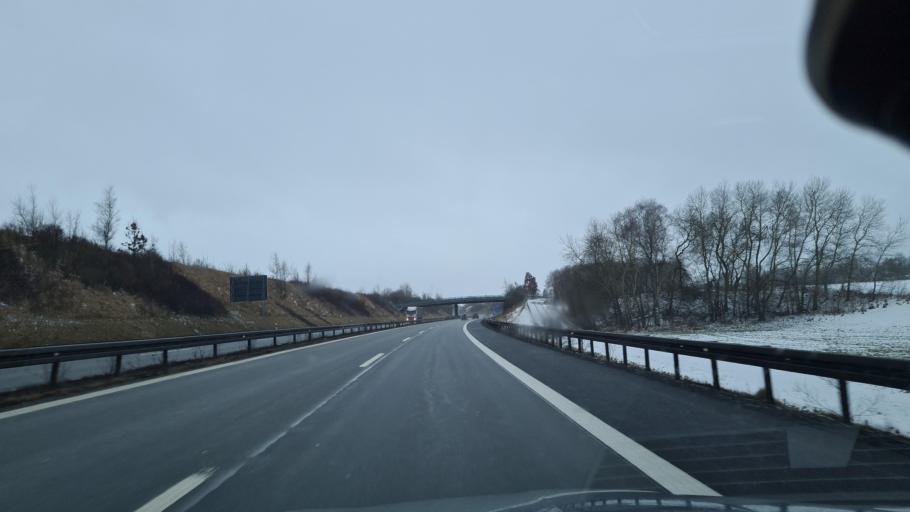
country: DE
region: Bavaria
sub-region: Upper Franconia
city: Thierstein
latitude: 50.1108
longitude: 12.0962
